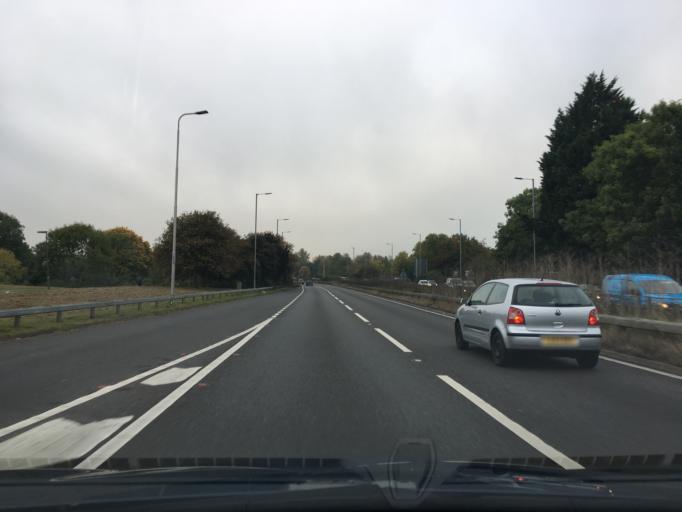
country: GB
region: England
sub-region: Surrey
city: Guildford
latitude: 51.2422
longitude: -0.5974
